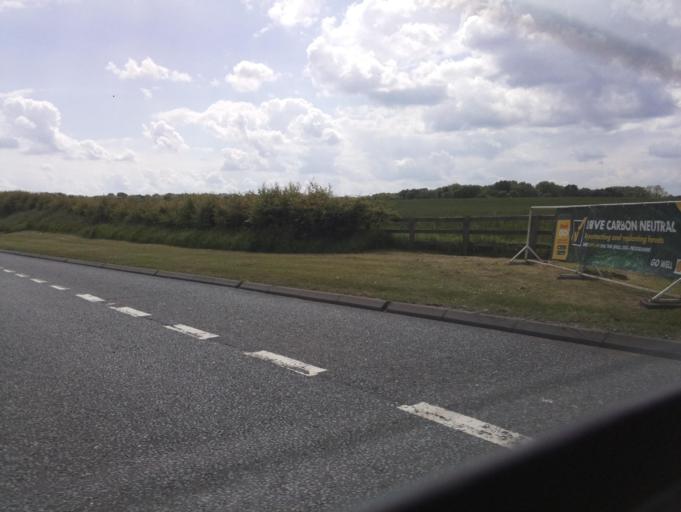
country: GB
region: England
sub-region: Hartlepool
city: Elwick
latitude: 54.6537
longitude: -1.3031
